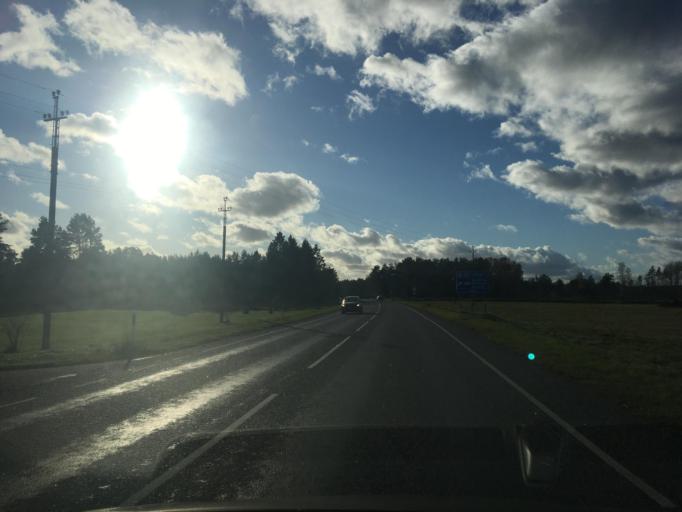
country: EE
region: Laeaene
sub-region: Lihula vald
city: Lihula
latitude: 58.6650
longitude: 23.7396
